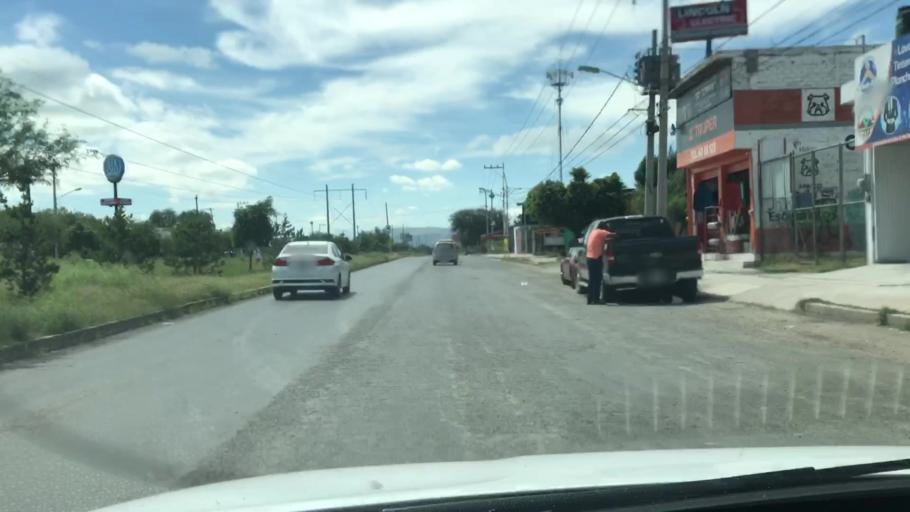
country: MX
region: Guanajuato
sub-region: Celaya
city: La Trinidad
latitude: 20.5452
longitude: -100.7805
